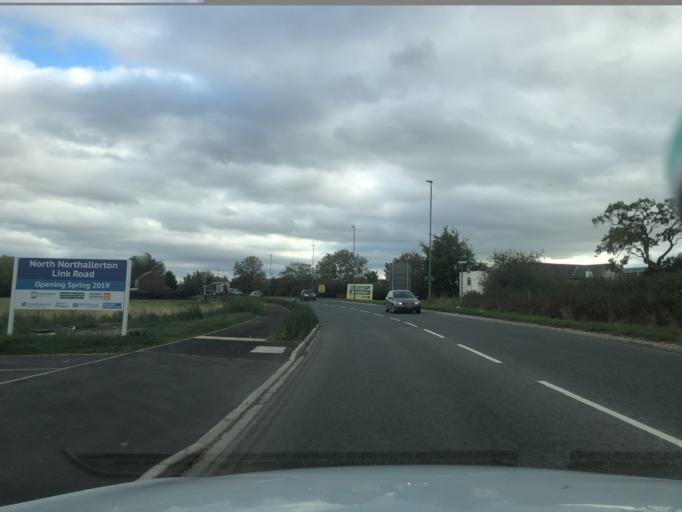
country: GB
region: England
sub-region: North Yorkshire
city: Northallerton
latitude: 54.3528
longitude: -1.4481
